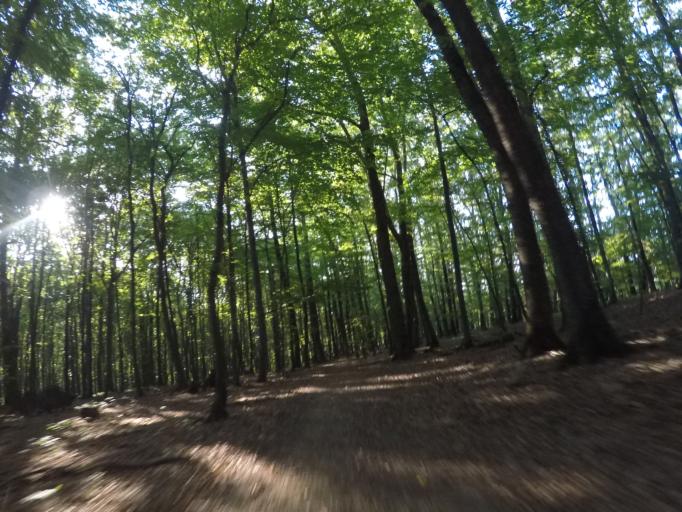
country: SK
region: Kosicky
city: Kosice
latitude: 48.7263
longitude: 21.1584
